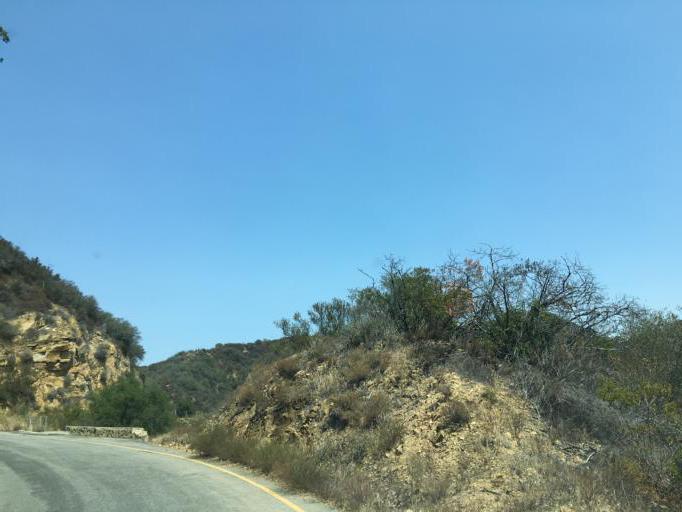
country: US
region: California
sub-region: Los Angeles County
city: Topanga
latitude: 34.0577
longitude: -118.6012
